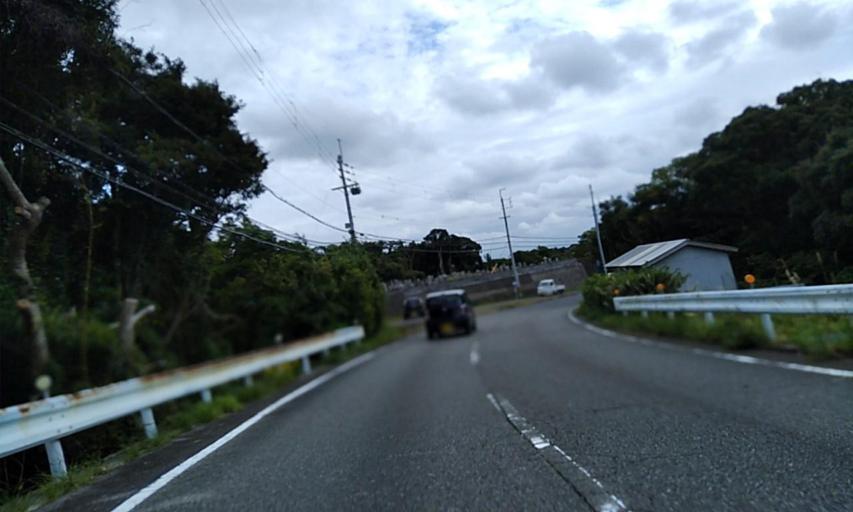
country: JP
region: Wakayama
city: Shingu
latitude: 33.4701
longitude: 135.8468
